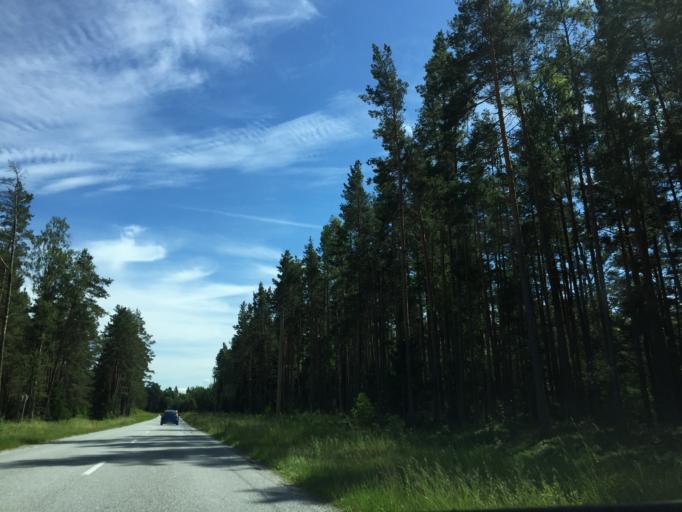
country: LV
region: Talsu Rajons
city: Valdemarpils
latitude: 57.5928
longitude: 22.6079
